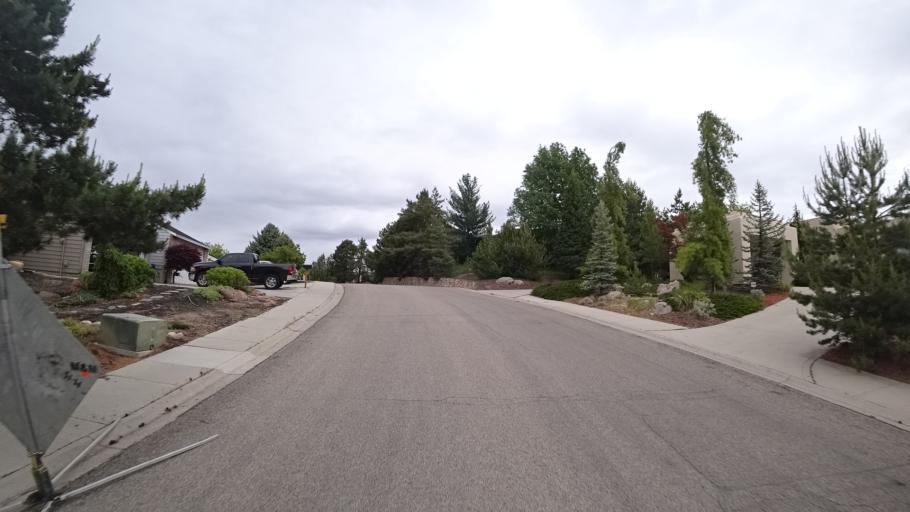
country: US
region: Idaho
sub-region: Ada County
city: Boise
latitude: 43.6159
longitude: -116.1717
